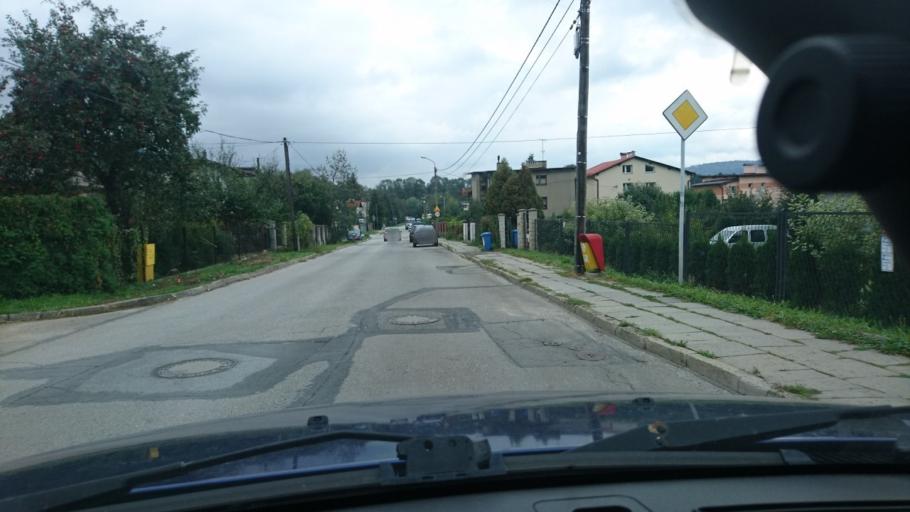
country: PL
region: Silesian Voivodeship
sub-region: Bielsko-Biala
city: Bielsko-Biala
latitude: 49.8041
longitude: 19.0686
